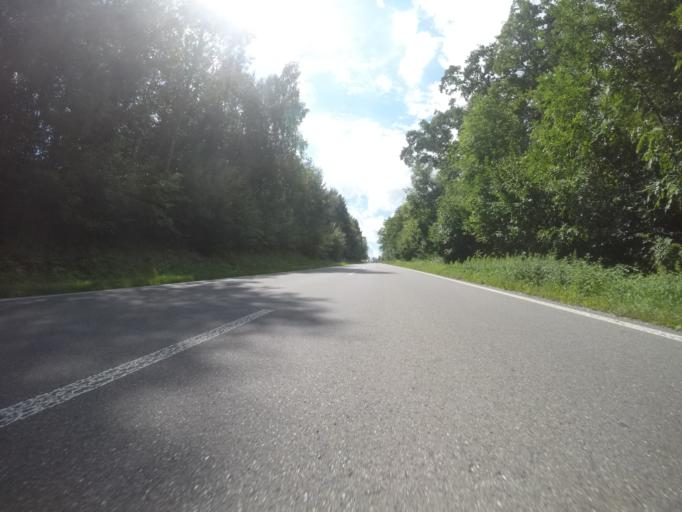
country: DE
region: Baden-Wuerttemberg
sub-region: Karlsruhe Region
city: Neubulach
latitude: 48.6683
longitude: 8.6895
